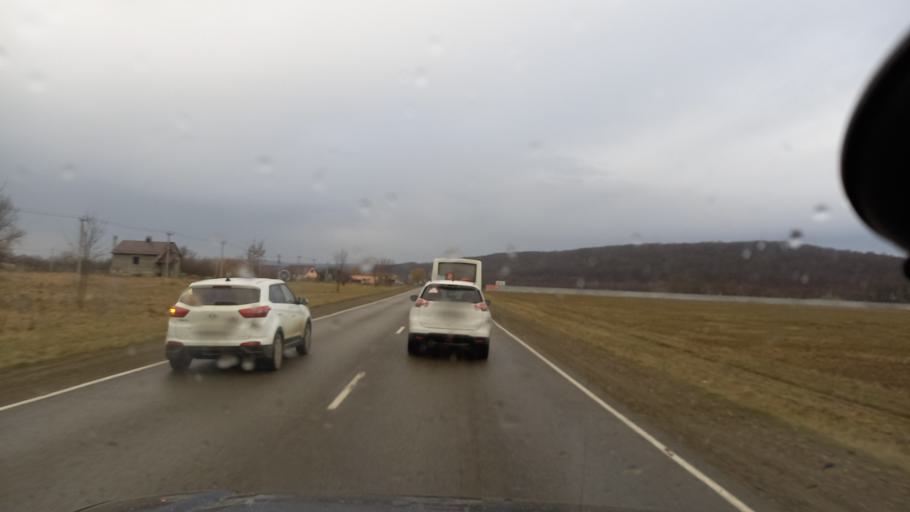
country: RU
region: Adygeya
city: Tul'skiy
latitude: 44.5299
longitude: 40.1372
